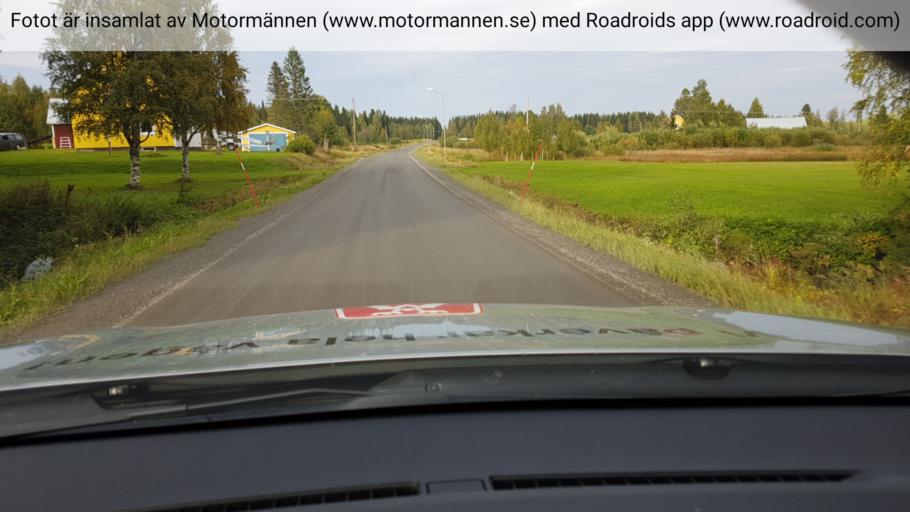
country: SE
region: Jaemtland
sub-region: Stroemsunds Kommun
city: Stroemsund
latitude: 64.0537
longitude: 15.8113
